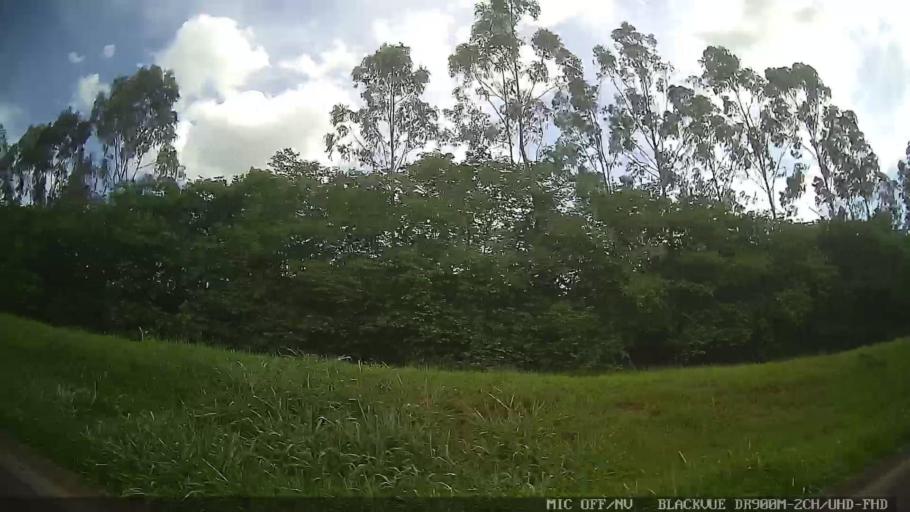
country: BR
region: Sao Paulo
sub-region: Conchas
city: Conchas
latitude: -23.0463
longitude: -47.9266
